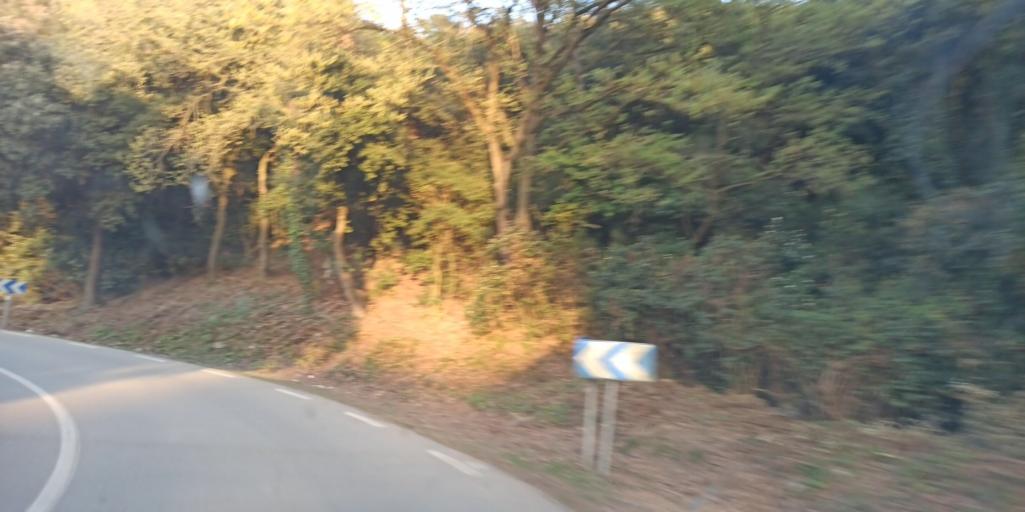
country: ES
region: Catalonia
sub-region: Provincia de Barcelona
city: Sarria-Sant Gervasi
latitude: 41.4457
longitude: 2.1304
